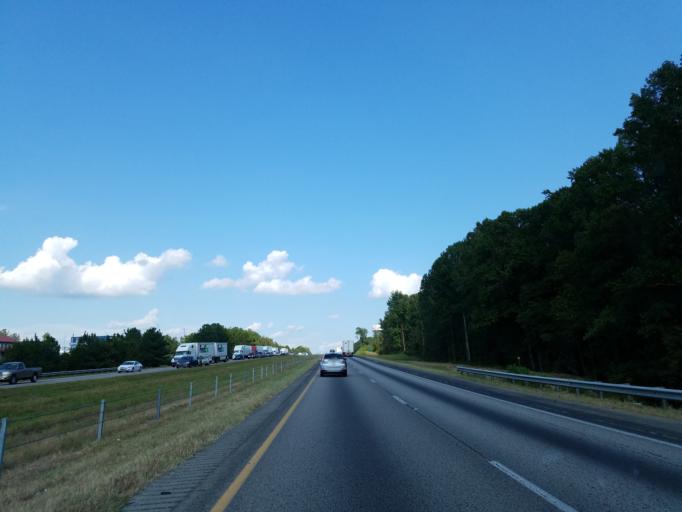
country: US
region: Georgia
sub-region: Jackson County
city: Jefferson
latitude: 34.1765
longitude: -83.6088
